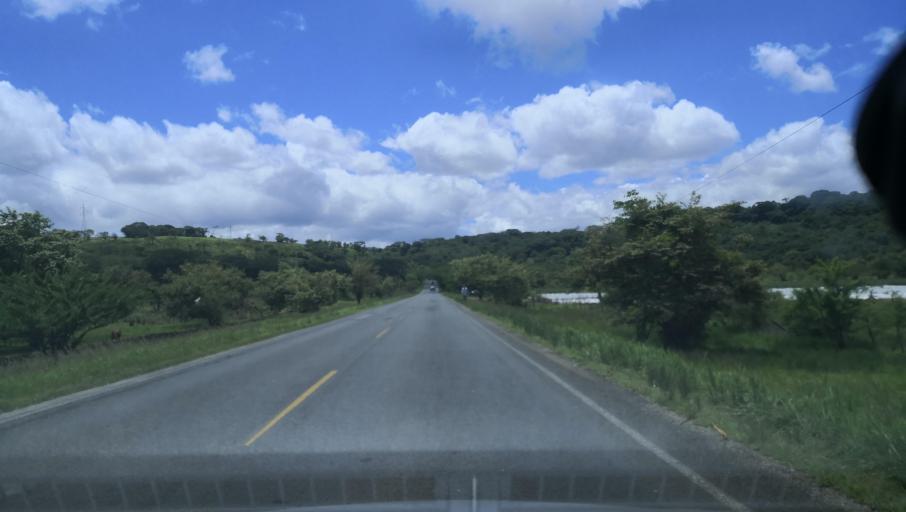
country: NI
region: Esteli
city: Esteli
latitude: 13.2034
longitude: -86.3755
